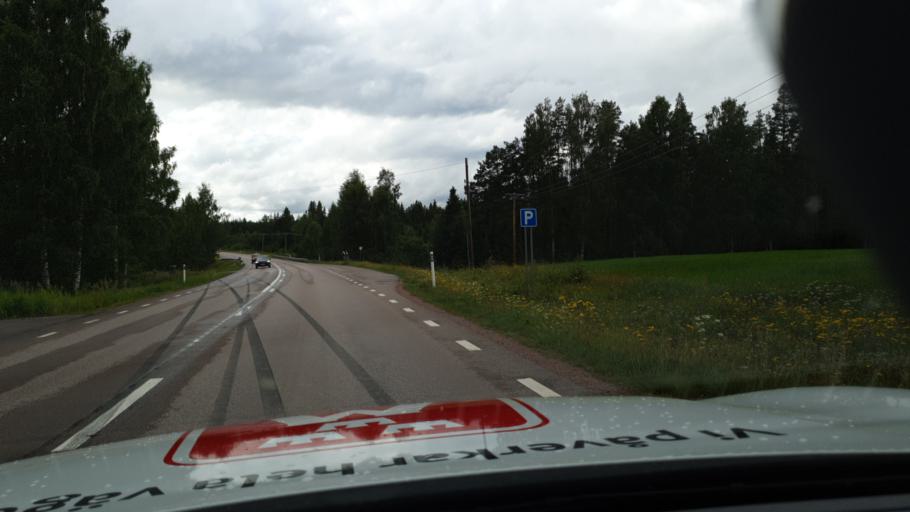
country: SE
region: Jaemtland
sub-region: Braecke Kommun
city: Braecke
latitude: 63.1659
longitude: 15.6876
